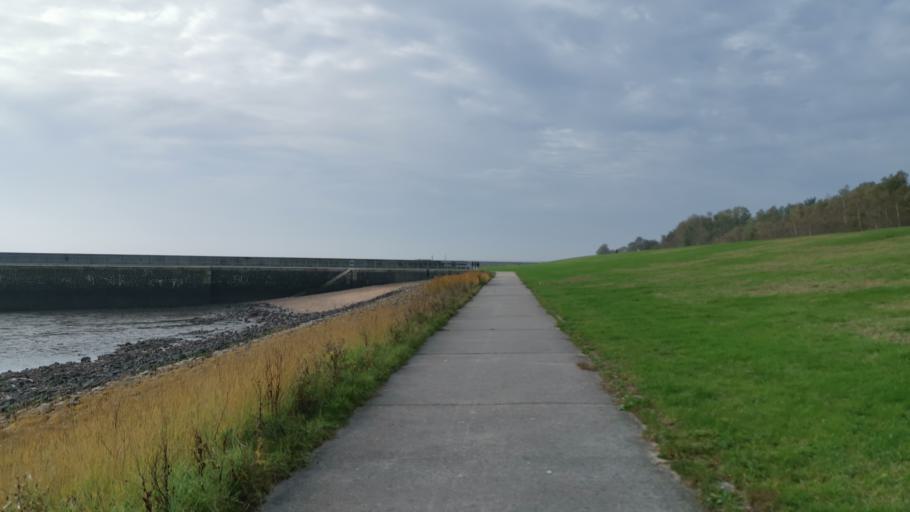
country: DE
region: Lower Saxony
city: Wilhelmshaven
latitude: 53.5191
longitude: 8.1601
